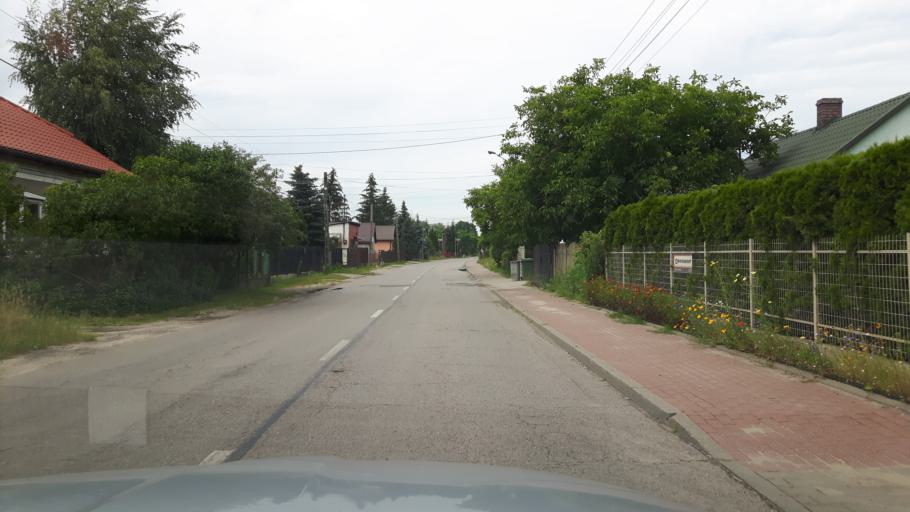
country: PL
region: Masovian Voivodeship
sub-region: Powiat wolominski
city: Kobylka
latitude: 52.3135
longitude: 21.2030
